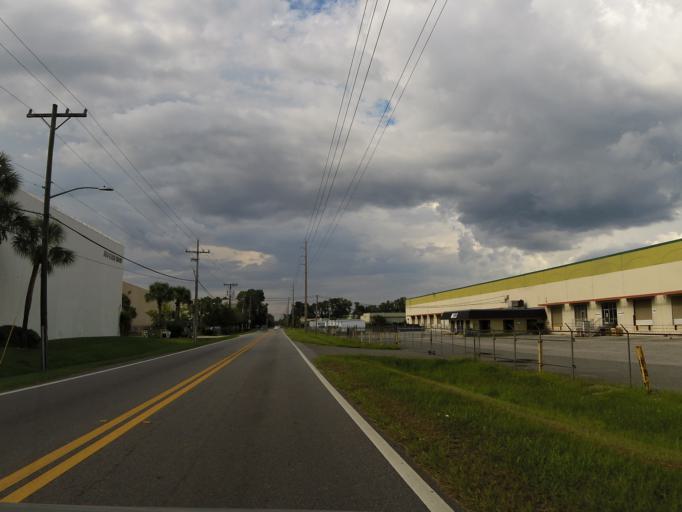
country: US
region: Florida
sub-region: Duval County
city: Jacksonville
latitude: 30.3306
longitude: -81.7435
